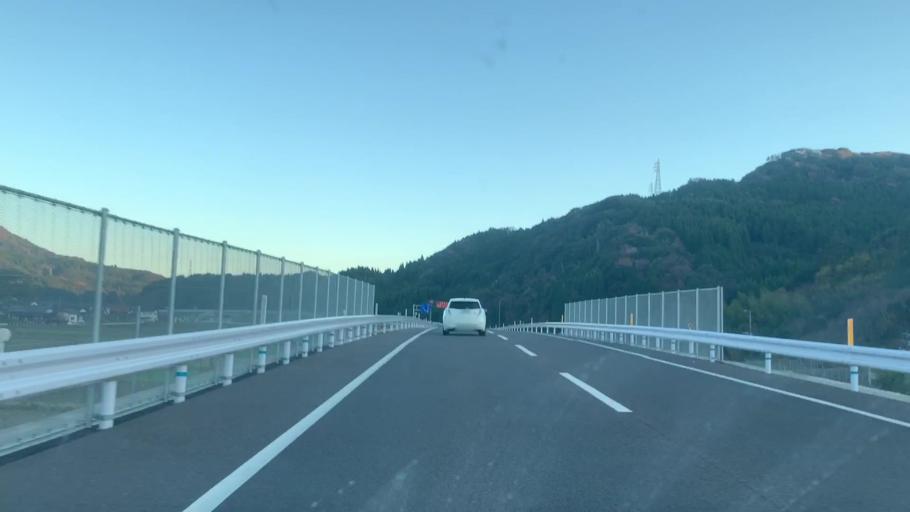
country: JP
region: Saga Prefecture
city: Takeocho-takeo
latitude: 33.2525
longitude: 129.9899
